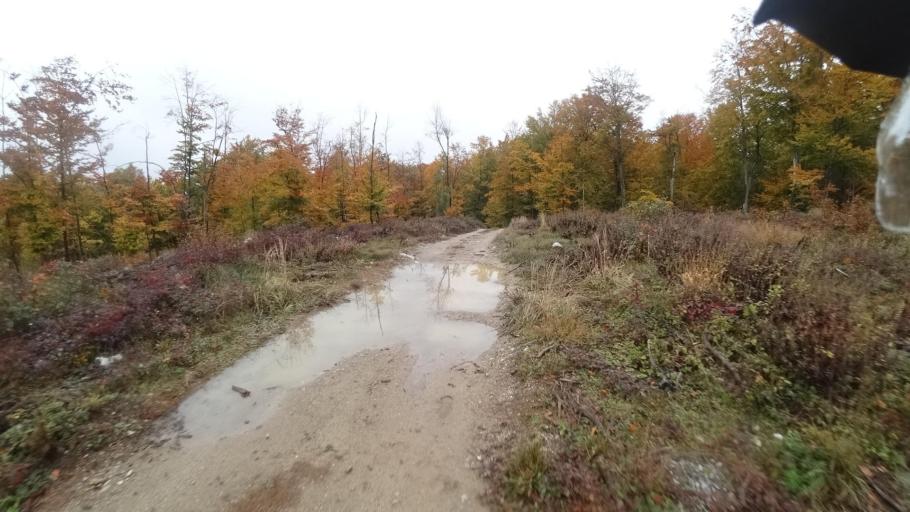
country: HR
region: Primorsko-Goranska
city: Vrbovsko
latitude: 45.4800
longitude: 15.0400
